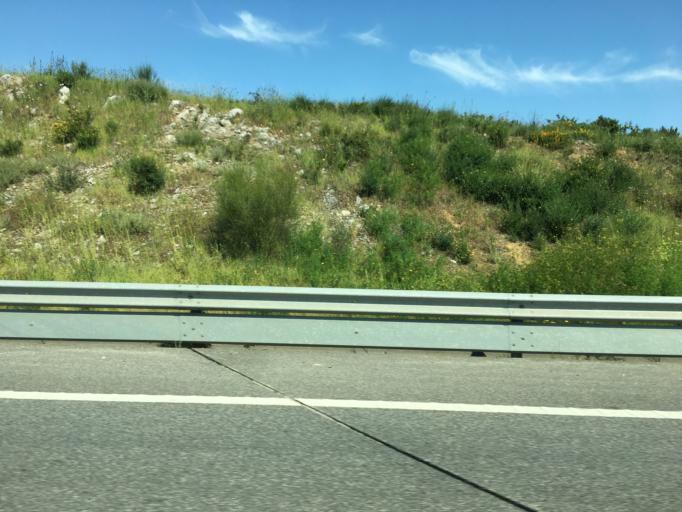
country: PT
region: Lisbon
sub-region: Sintra
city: Sintra
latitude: 38.8059
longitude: -9.3603
